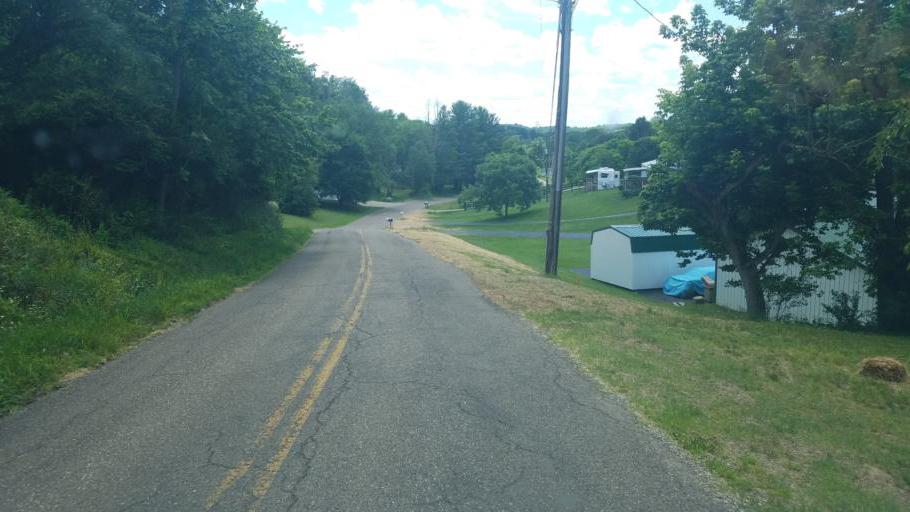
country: US
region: Ohio
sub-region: Gallia County
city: Gallipolis
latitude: 38.7994
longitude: -82.2278
